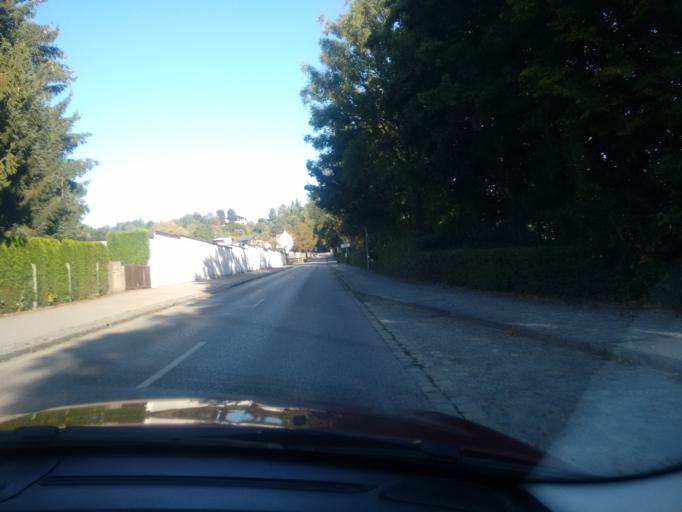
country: DE
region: Bavaria
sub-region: Upper Bavaria
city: Burghausen
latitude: 48.1549
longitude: 12.8225
